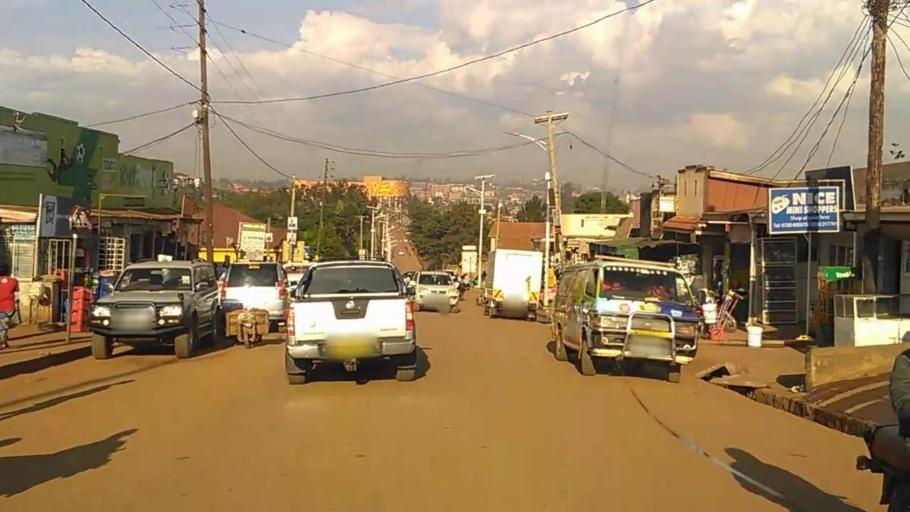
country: UG
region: Central Region
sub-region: Kampala District
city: Kampala
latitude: 0.3094
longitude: 32.5925
